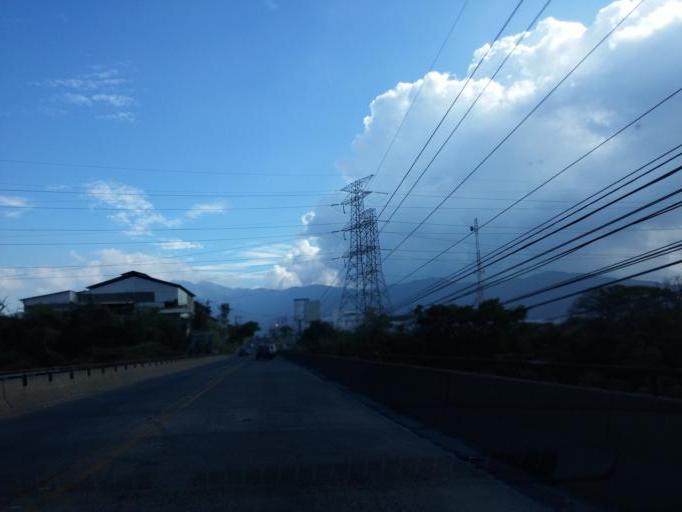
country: CR
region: Heredia
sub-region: Canton de Belen
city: San Antonio
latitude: 9.9660
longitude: -84.1992
